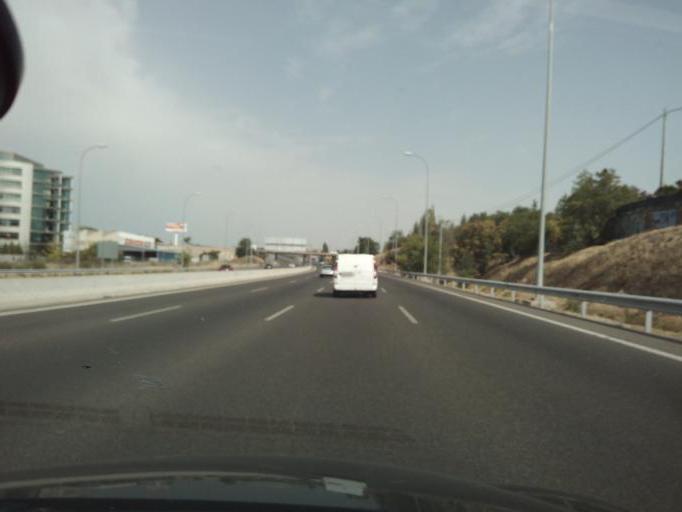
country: ES
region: Madrid
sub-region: Provincia de Madrid
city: Hortaleza
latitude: 40.4765
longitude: -3.6316
